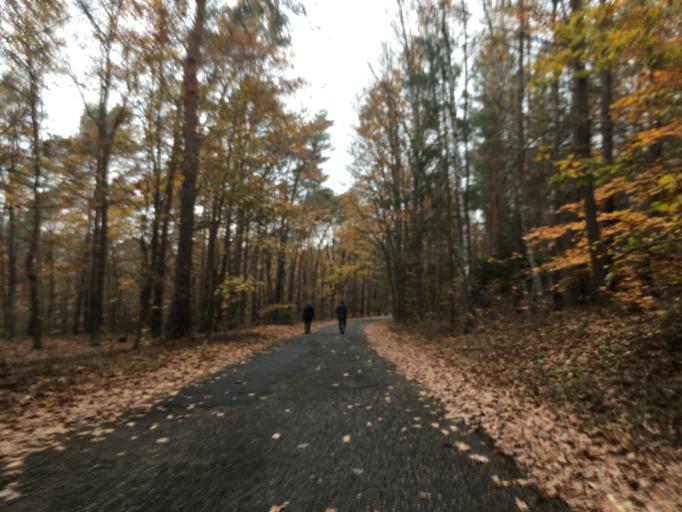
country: DE
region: Brandenburg
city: Mixdorf
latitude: 52.1769
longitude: 14.4351
